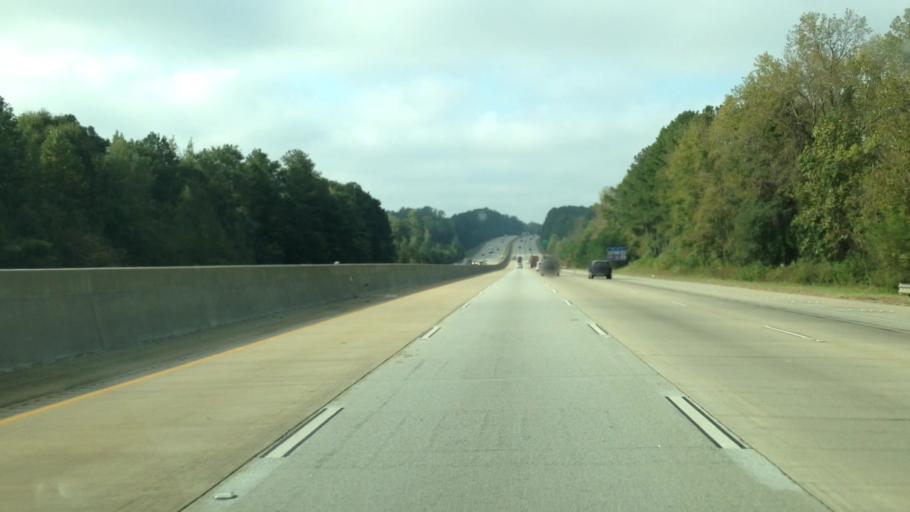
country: US
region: Georgia
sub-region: Coweta County
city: Newnan
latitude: 33.4161
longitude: -84.7321
